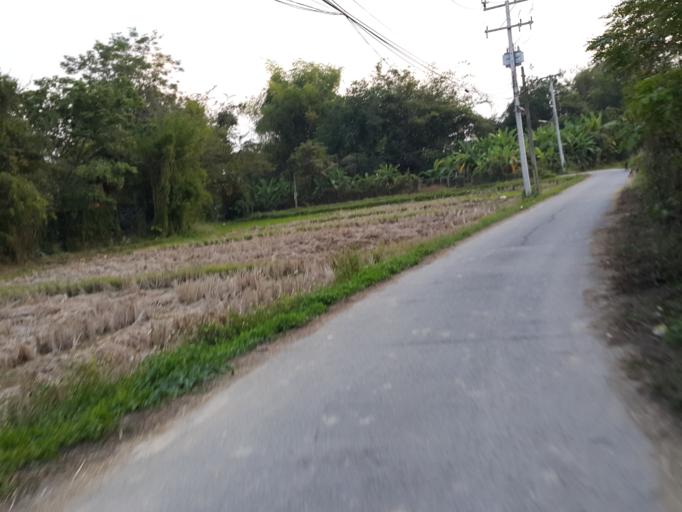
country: TH
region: Chiang Mai
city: San Sai
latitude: 18.8364
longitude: 99.1077
